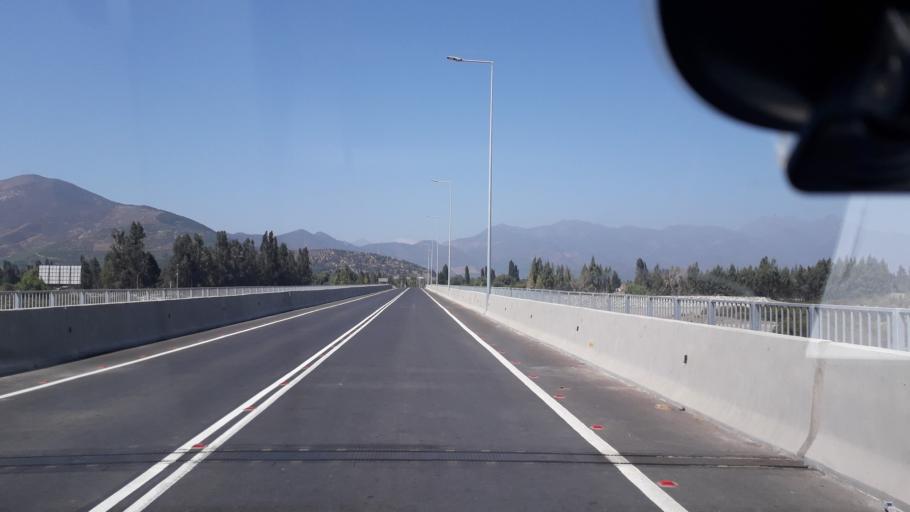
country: CL
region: Valparaiso
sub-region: Provincia de Quillota
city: Hacienda La Calera
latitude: -32.8159
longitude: -71.2449
